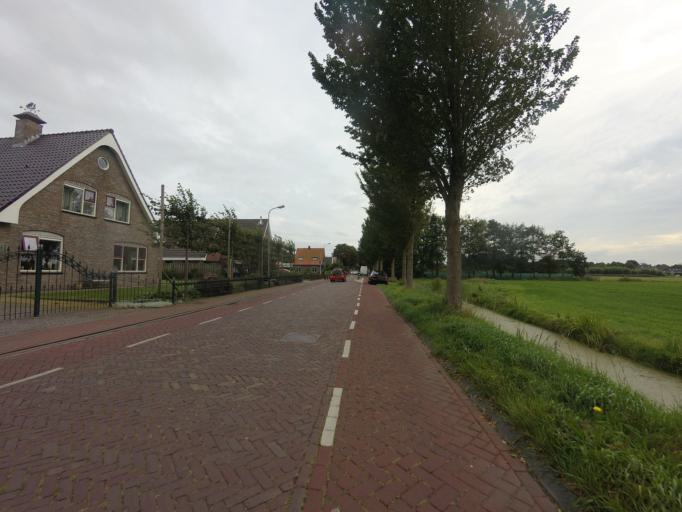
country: NL
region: North Holland
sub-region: Gemeente Medemblik
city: Opperdoes
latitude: 52.7074
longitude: 5.0576
